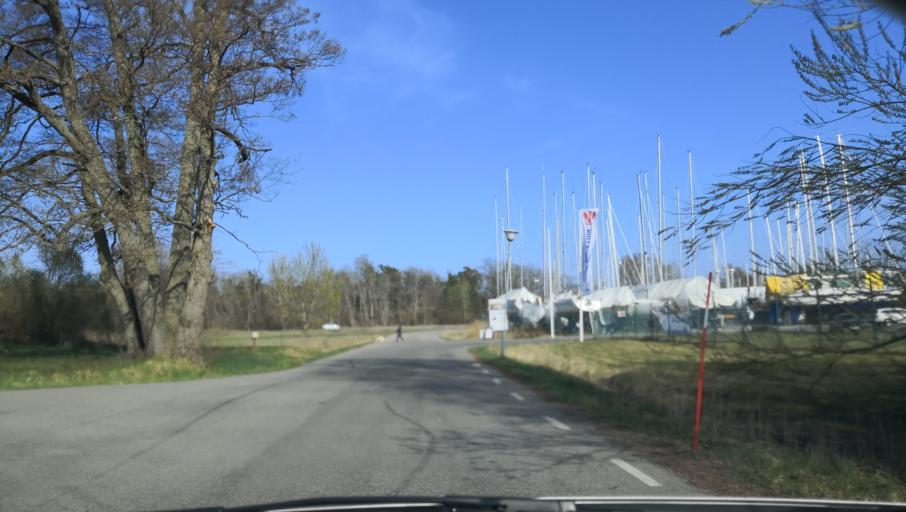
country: SE
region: Stockholm
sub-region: Varmdo Kommun
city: Holo
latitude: 59.3020
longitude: 18.6490
